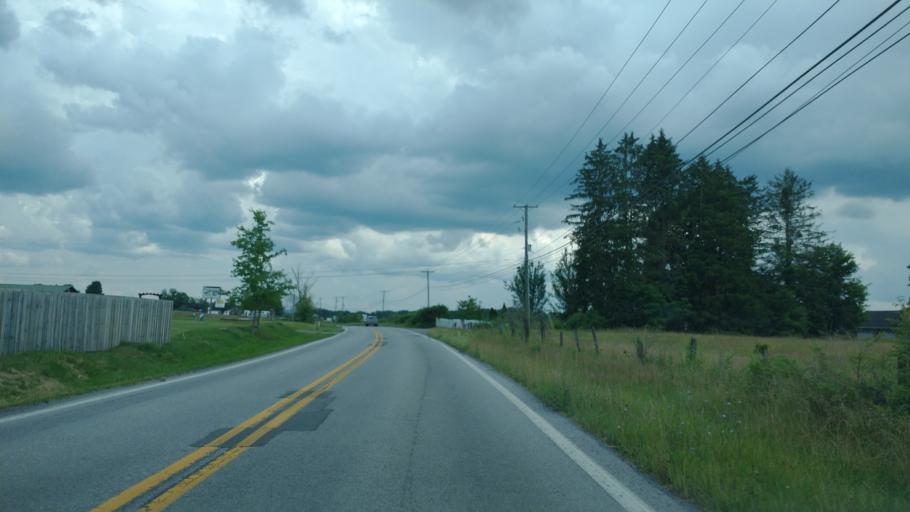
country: US
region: West Virginia
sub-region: Mercer County
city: Athens
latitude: 37.4556
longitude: -81.0098
